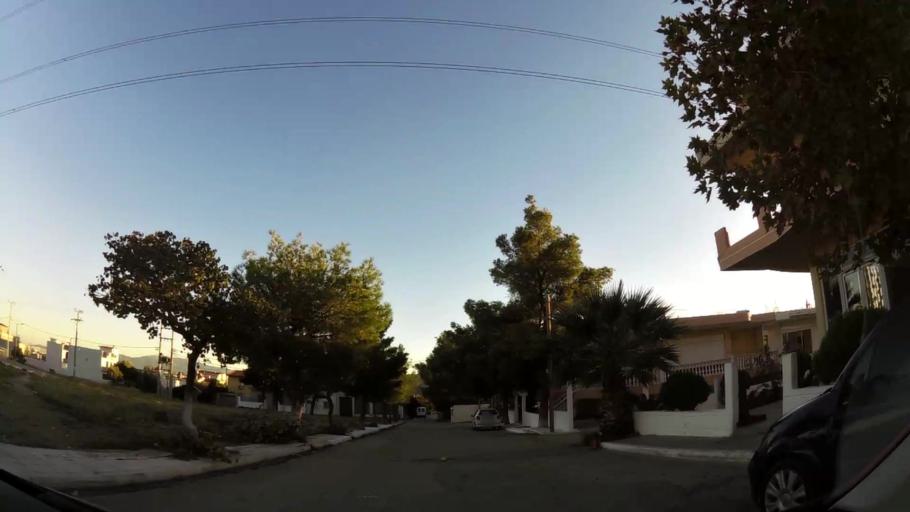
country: GR
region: Attica
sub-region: Nomarchia Dytikis Attikis
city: Ano Liosia
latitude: 38.0893
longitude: 23.6898
